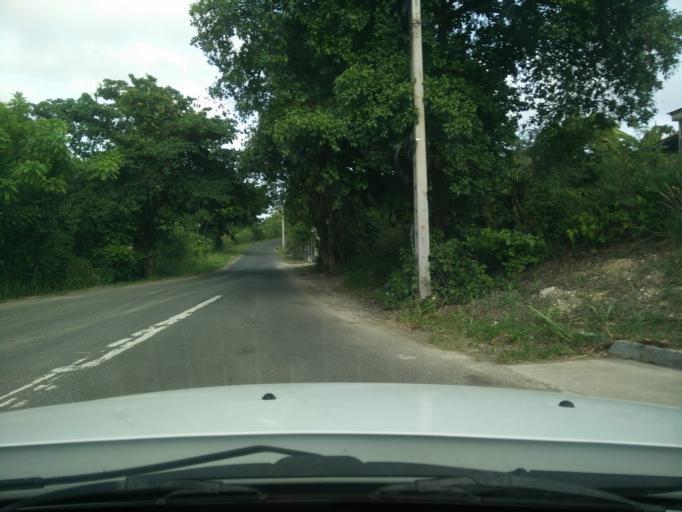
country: GP
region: Guadeloupe
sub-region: Guadeloupe
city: Sainte-Anne
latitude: 16.2530
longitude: -61.3335
